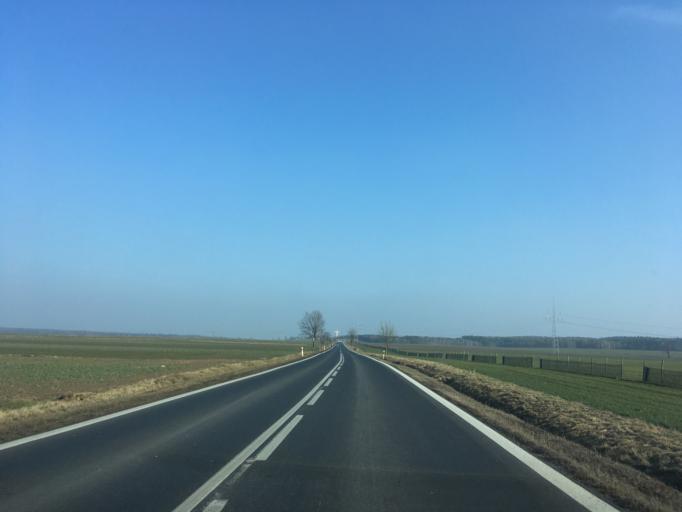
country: PL
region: Lower Silesian Voivodeship
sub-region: Powiat zlotoryjski
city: Olszanica
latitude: 51.2640
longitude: 15.7272
